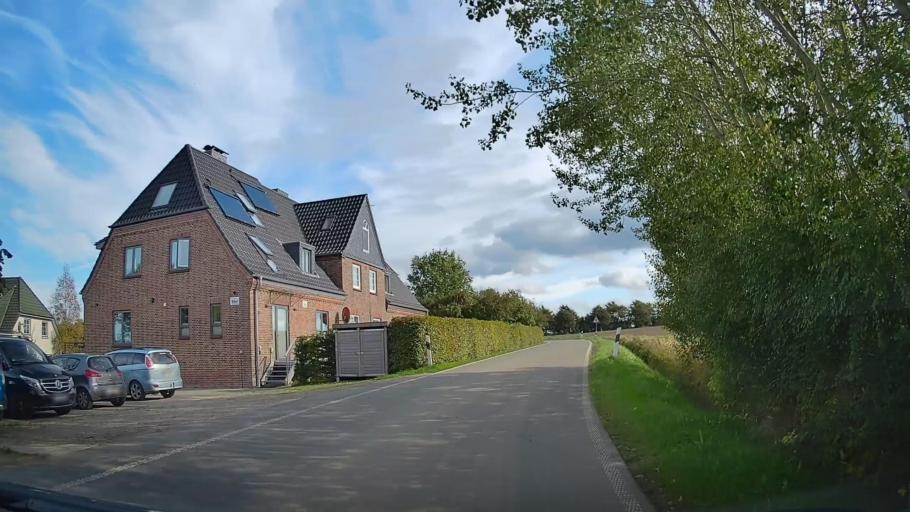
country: DE
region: Schleswig-Holstein
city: Steinbergkirche
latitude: 54.8019
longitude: 9.7425
